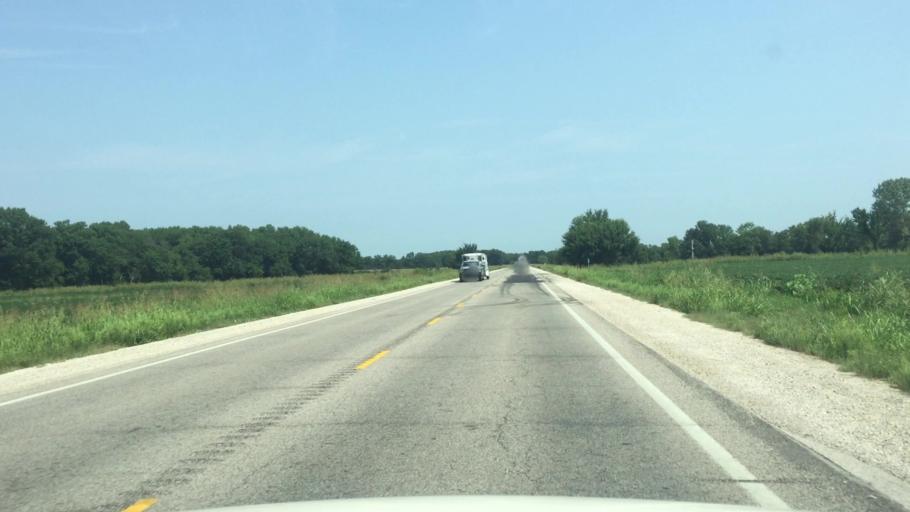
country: US
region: Kansas
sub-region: Montgomery County
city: Cherryvale
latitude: 37.1656
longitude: -95.5766
